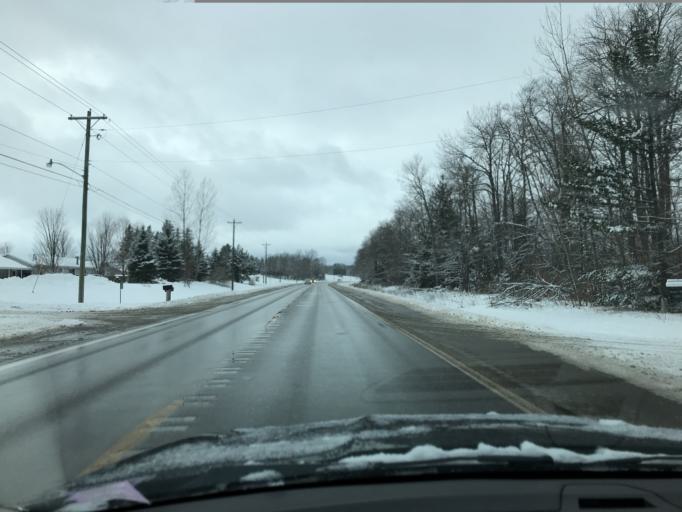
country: US
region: Michigan
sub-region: Charlevoix County
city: Charlevoix
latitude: 45.2807
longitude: -85.2343
